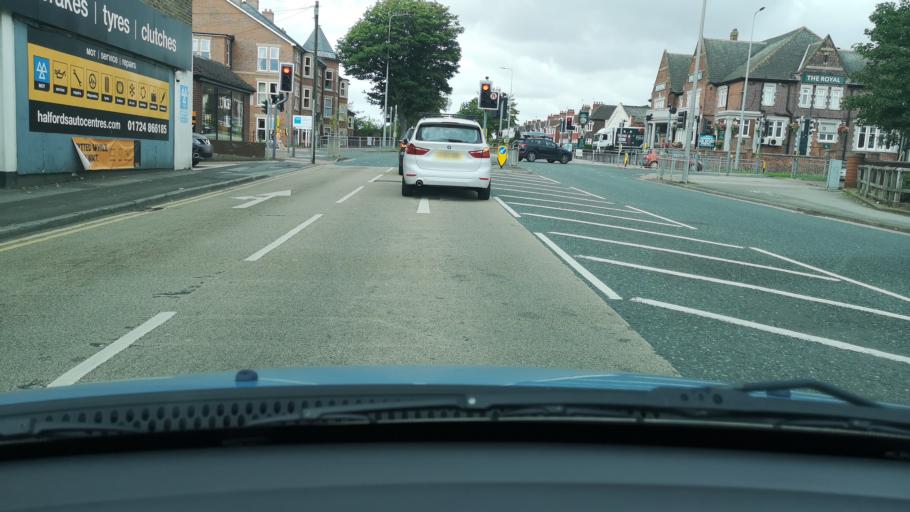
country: GB
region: England
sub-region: North Lincolnshire
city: Scunthorpe
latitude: 53.5906
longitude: -0.6603
